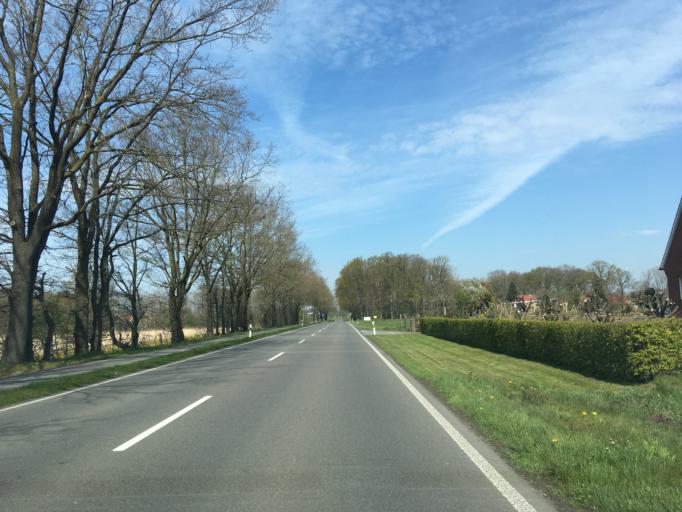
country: DE
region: North Rhine-Westphalia
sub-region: Regierungsbezirk Munster
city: Vreden
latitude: 52.0144
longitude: 6.8511
